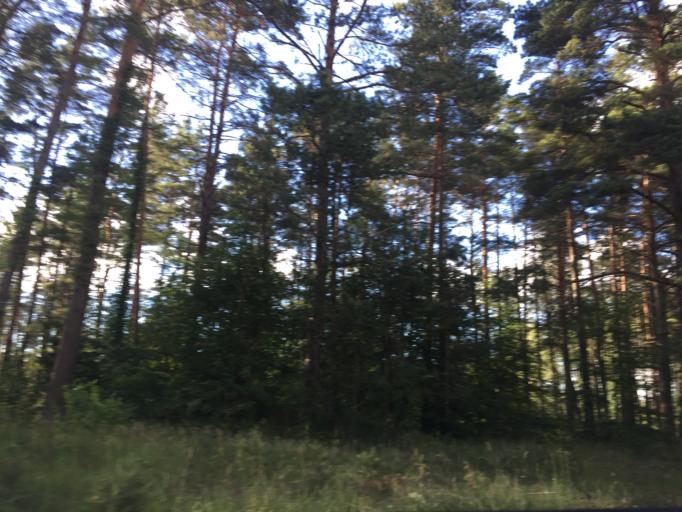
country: LV
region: Adazi
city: Adazi
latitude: 57.1299
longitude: 24.3478
